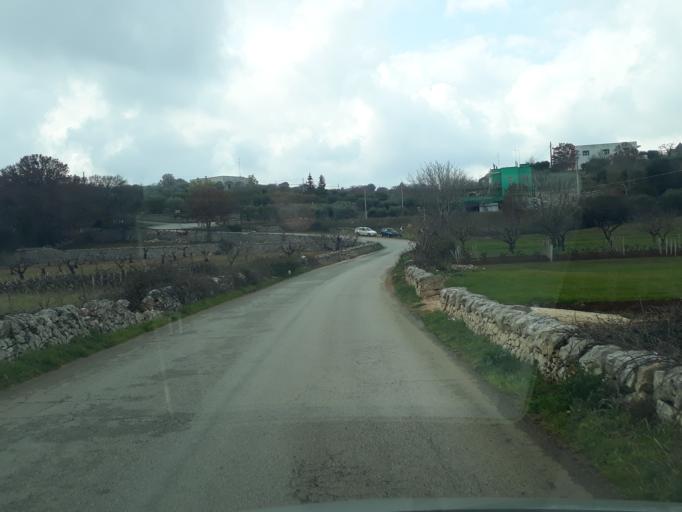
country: IT
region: Apulia
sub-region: Provincia di Brindisi
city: Lamie di Olimpie-Selva
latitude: 40.7904
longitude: 17.3309
